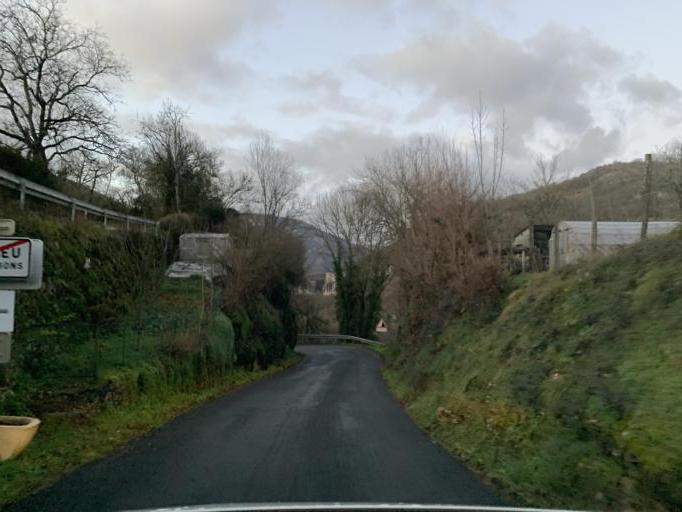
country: FR
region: Rhone-Alpes
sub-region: Departement de l'Ain
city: Virieu-le-Grand
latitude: 45.8113
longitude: 5.6584
